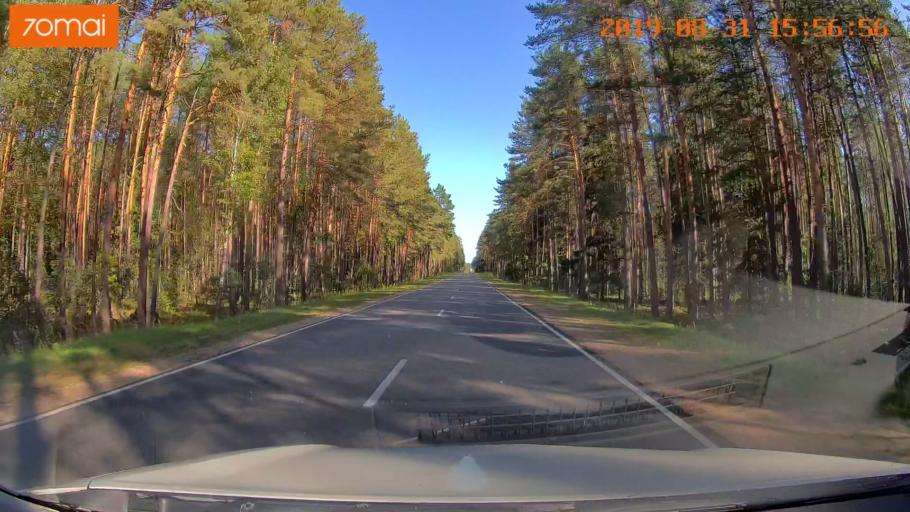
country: RU
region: Kaluga
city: Yukhnov
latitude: 54.7272
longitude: 35.1957
